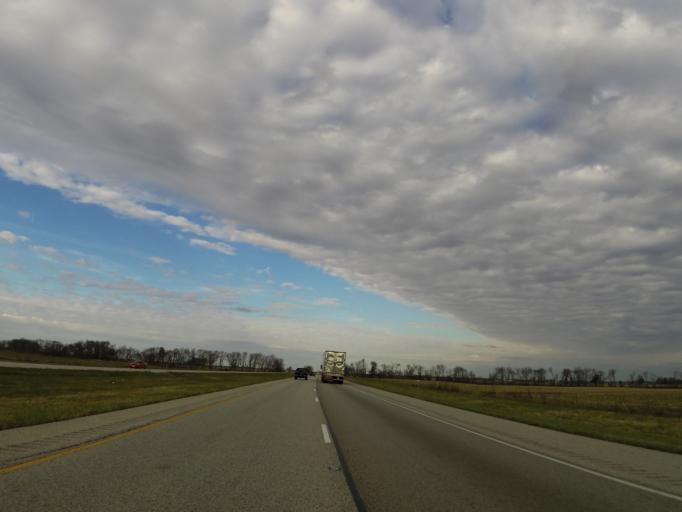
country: US
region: Illinois
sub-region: Washington County
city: Nashville
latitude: 38.4155
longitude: -89.4401
